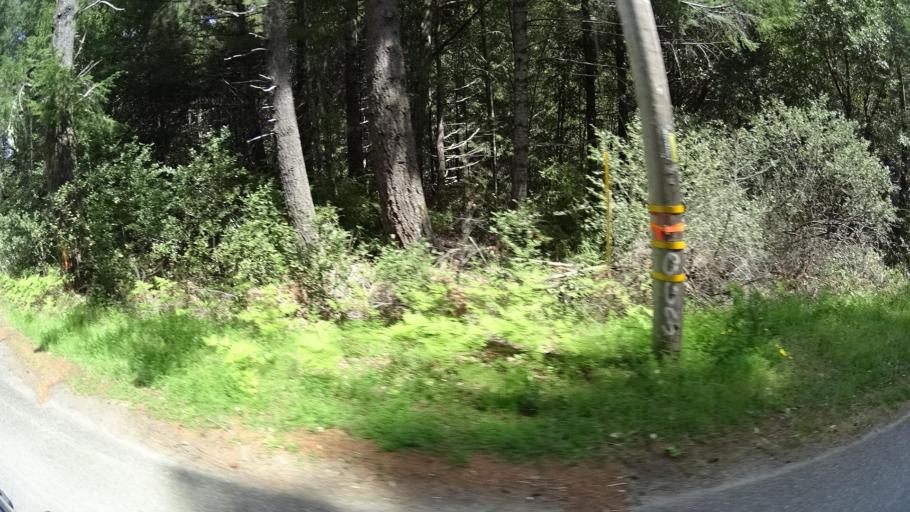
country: US
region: California
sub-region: Humboldt County
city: Redway
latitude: 40.0739
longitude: -123.9573
